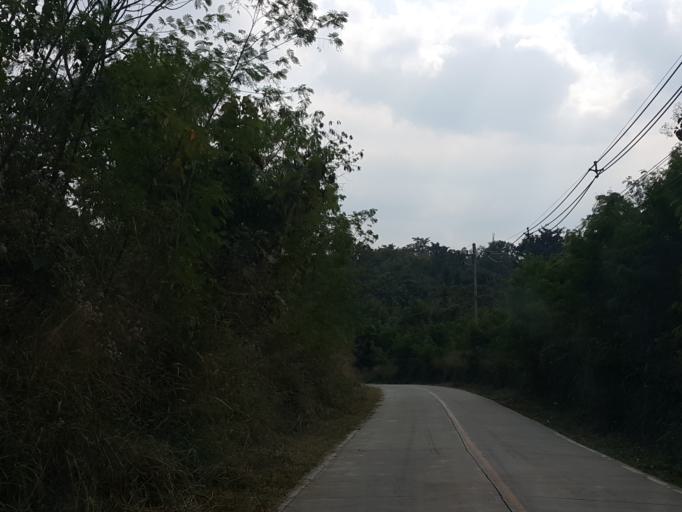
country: TH
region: Chiang Mai
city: Mae On
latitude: 18.8196
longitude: 99.2200
